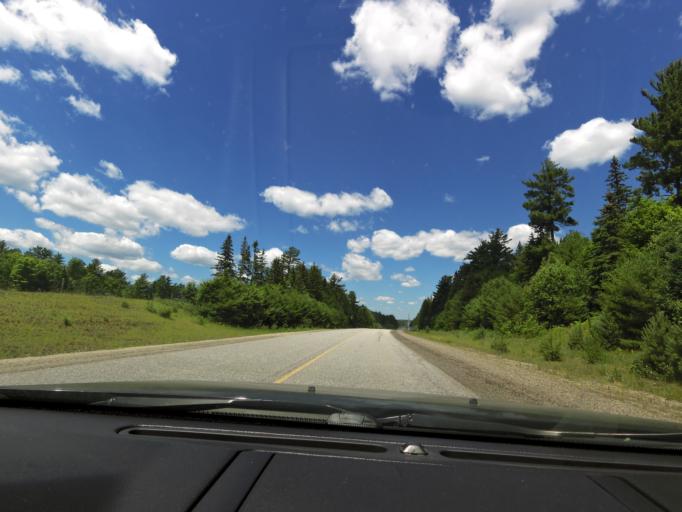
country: CA
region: Ontario
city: Huntsville
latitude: 45.5182
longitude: -79.3119
